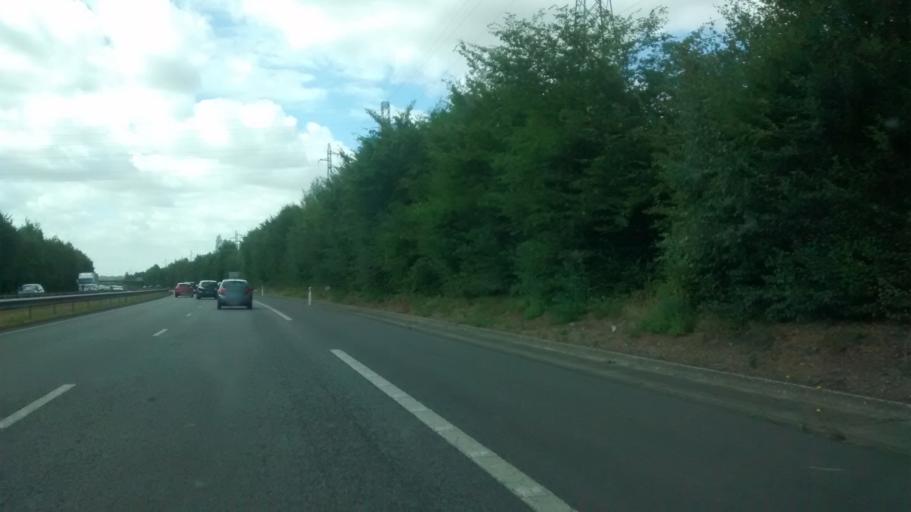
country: FR
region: Brittany
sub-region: Departement d'Ille-et-Vilaine
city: Betton
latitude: 48.1430
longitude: -1.6484
